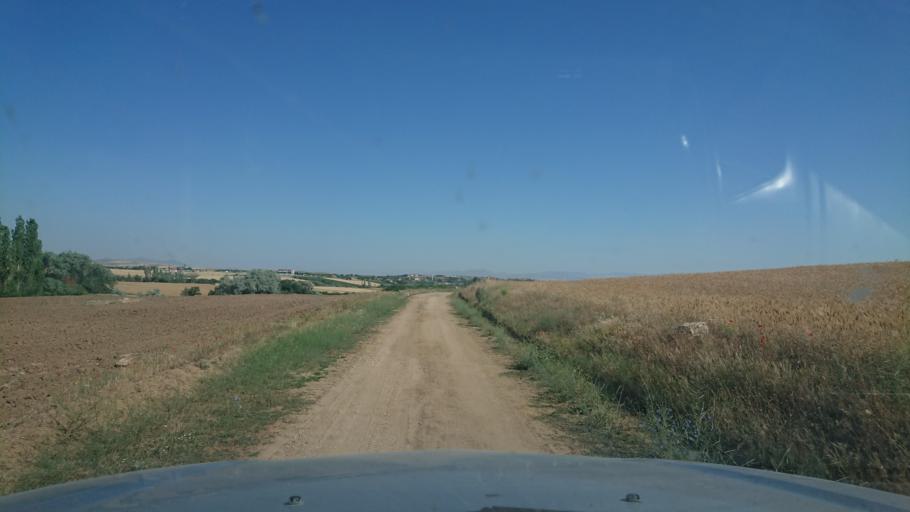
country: TR
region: Aksaray
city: Agacoren
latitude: 38.8518
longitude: 33.9148
